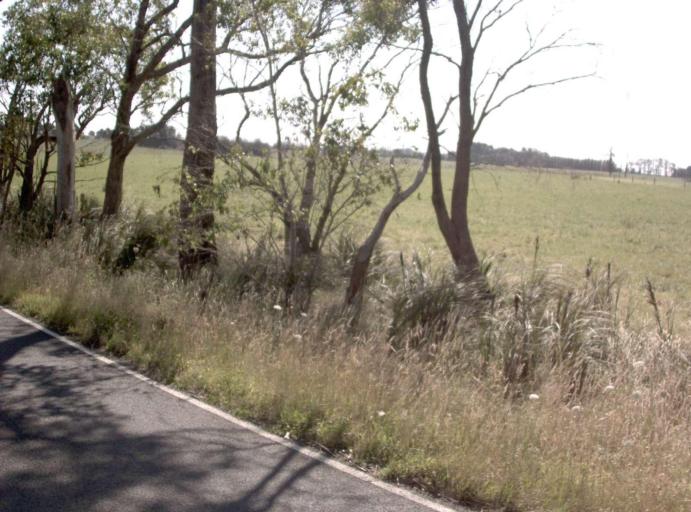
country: AU
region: Victoria
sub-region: Baw Baw
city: Warragul
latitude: -38.2098
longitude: 145.8103
